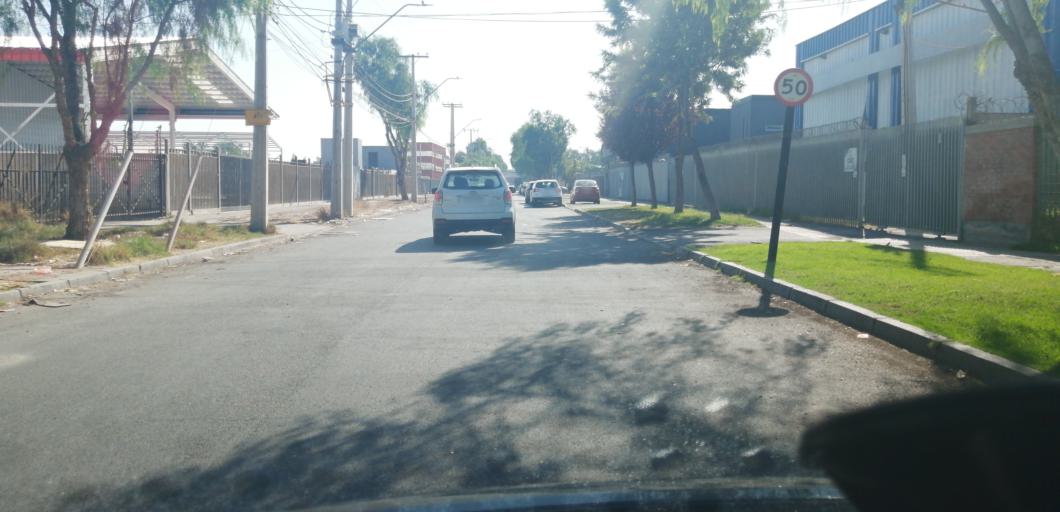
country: CL
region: Santiago Metropolitan
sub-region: Provincia de Santiago
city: Lo Prado
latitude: -33.3849
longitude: -70.7775
